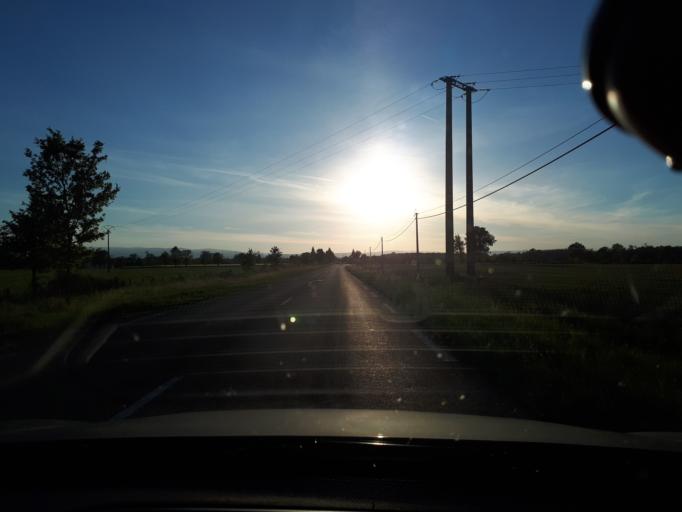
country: FR
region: Rhone-Alpes
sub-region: Departement de la Loire
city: Feurs
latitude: 45.7372
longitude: 4.2667
